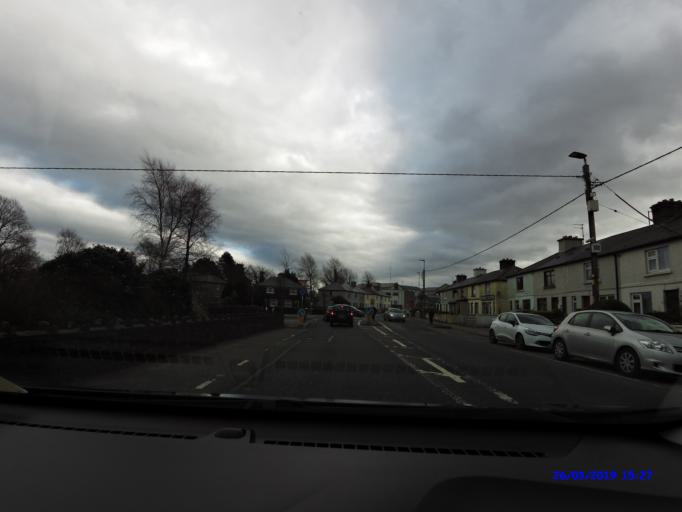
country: IE
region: Connaught
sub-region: Maigh Eo
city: Ballina
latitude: 54.1174
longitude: -9.1582
